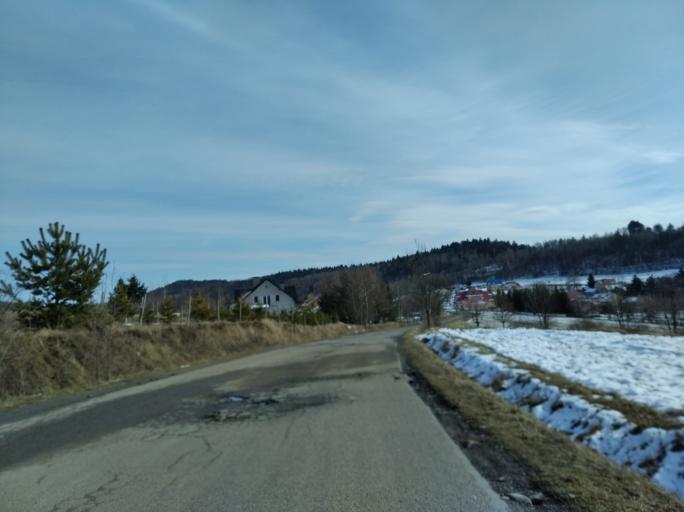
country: PL
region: Subcarpathian Voivodeship
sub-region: Powiat krosnienski
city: Korczyna
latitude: 49.7475
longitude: 21.7993
